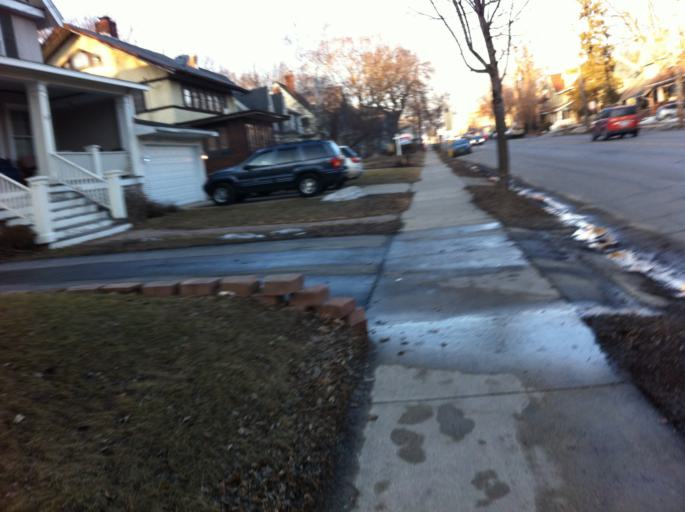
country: US
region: Wisconsin
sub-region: Dane County
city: Madison
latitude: 43.0633
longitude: -89.4221
